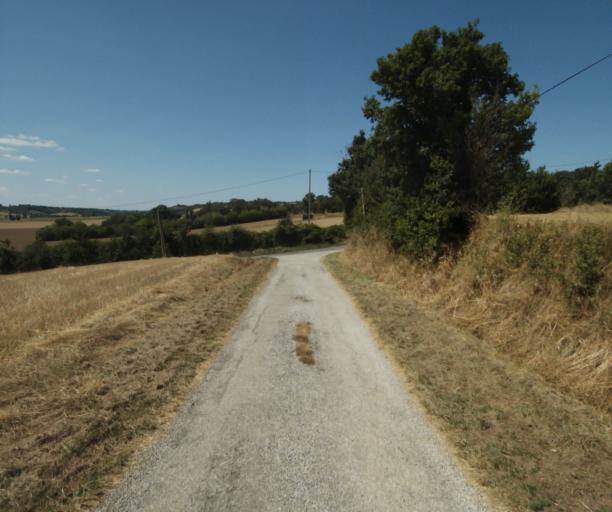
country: FR
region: Midi-Pyrenees
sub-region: Departement de la Haute-Garonne
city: Saint-Felix-Lauragais
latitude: 43.4893
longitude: 1.8874
